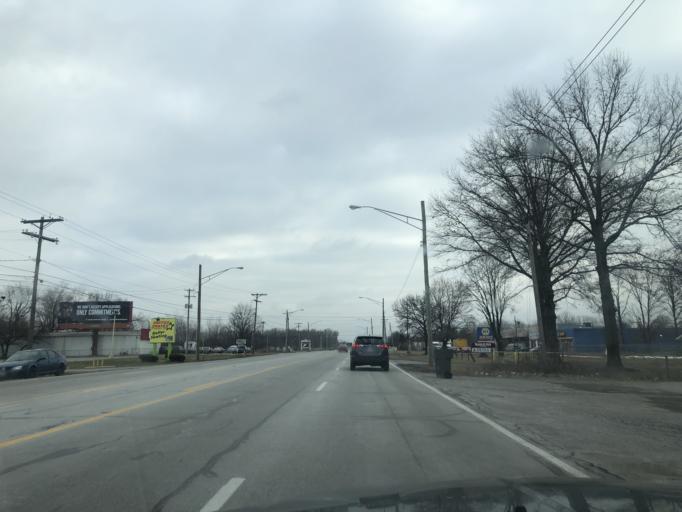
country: US
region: Ohio
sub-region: Franklin County
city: Groveport
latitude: 39.9173
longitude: -82.9133
